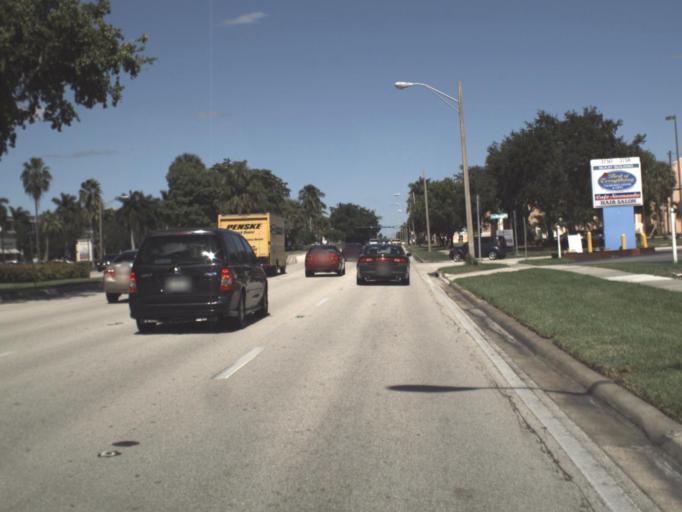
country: US
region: Florida
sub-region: Collier County
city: Pine Ridge
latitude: 26.1900
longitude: -81.7998
